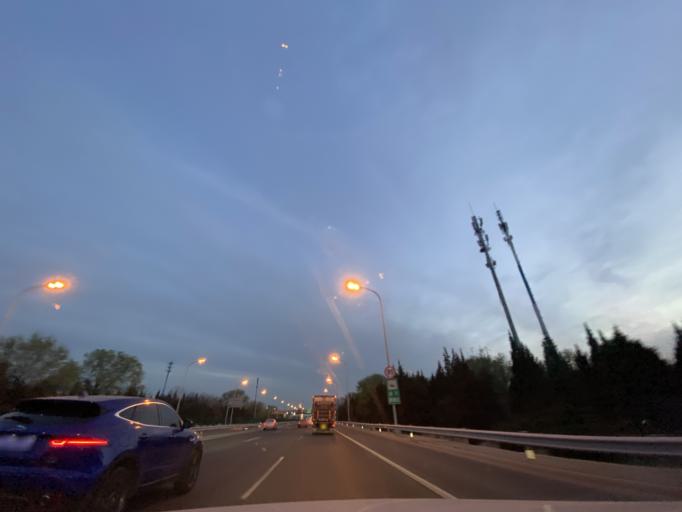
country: CN
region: Beijing
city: Xiangshan
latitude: 39.9620
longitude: 116.2118
